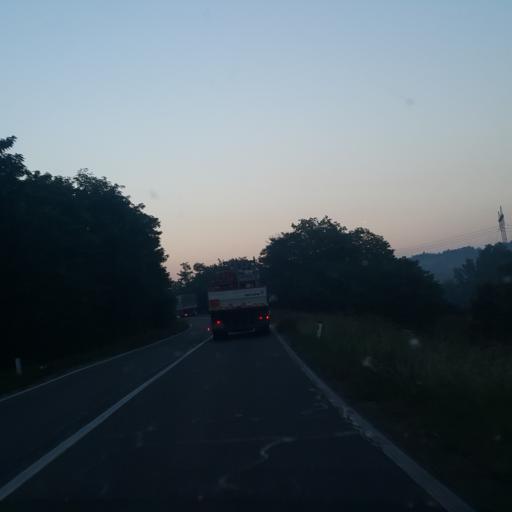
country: RS
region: Central Serbia
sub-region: Nisavski Okrug
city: Svrljig
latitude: 43.4293
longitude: 22.1496
